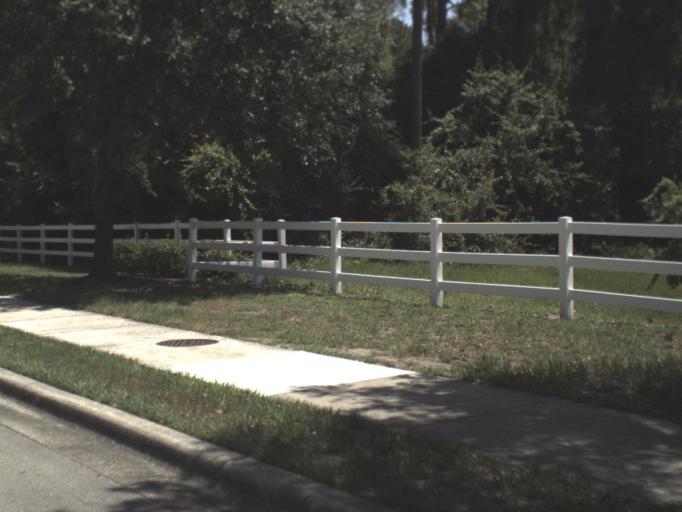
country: US
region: Florida
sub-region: Saint Johns County
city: Fruit Cove
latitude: 30.1113
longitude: -81.6262
